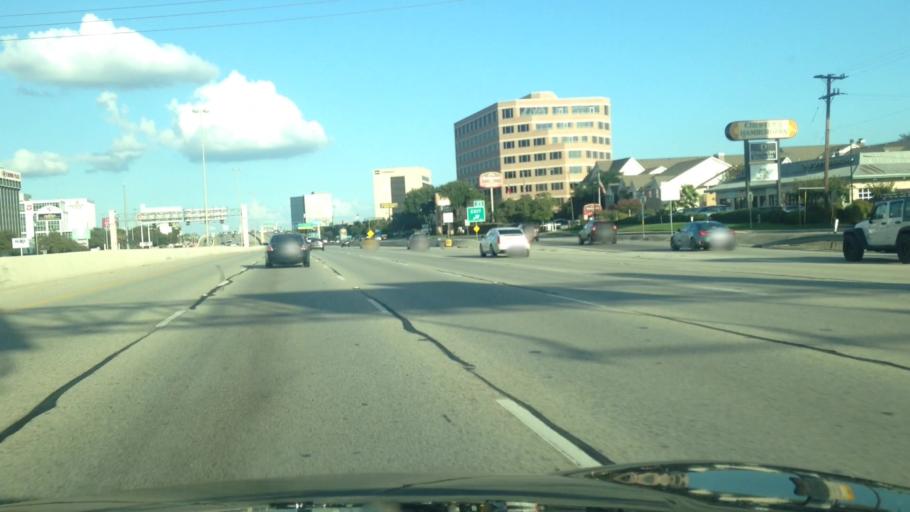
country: US
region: Texas
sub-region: Bexar County
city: Alamo Heights
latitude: 29.5163
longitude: -98.4596
